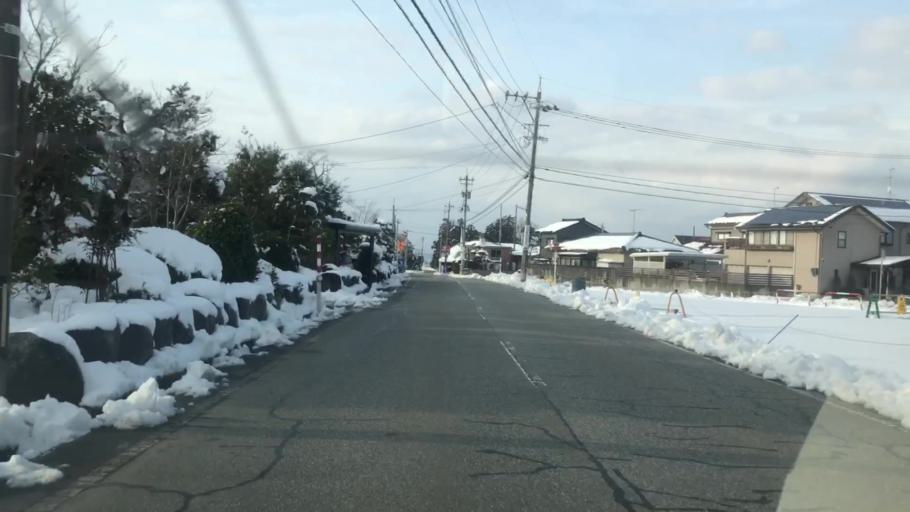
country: JP
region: Toyama
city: Toyama-shi
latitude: 36.6361
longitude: 137.2645
